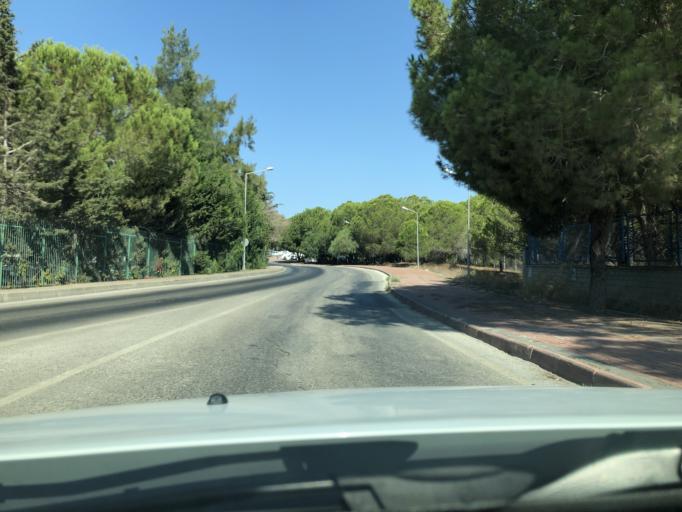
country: TR
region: Antalya
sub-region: Manavgat
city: Manavgat
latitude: 36.7585
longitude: 31.4362
